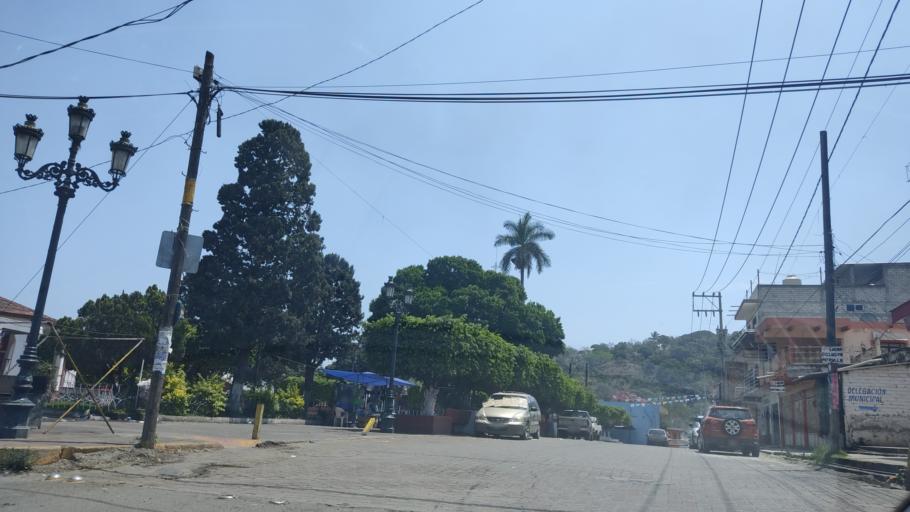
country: MX
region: Nayarit
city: Puga
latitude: 21.5838
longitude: -104.8226
